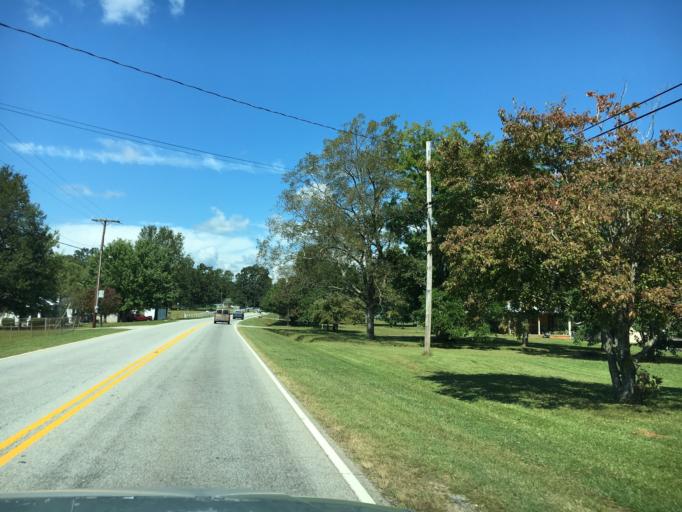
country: US
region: South Carolina
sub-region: Greenville County
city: Taylors
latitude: 34.9867
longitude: -82.3384
